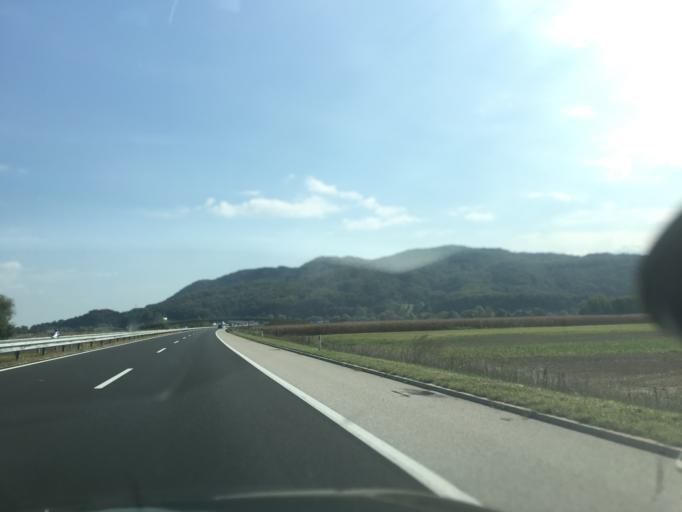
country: SI
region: Brezice
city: Brezice
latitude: 45.9009
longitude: 15.5729
